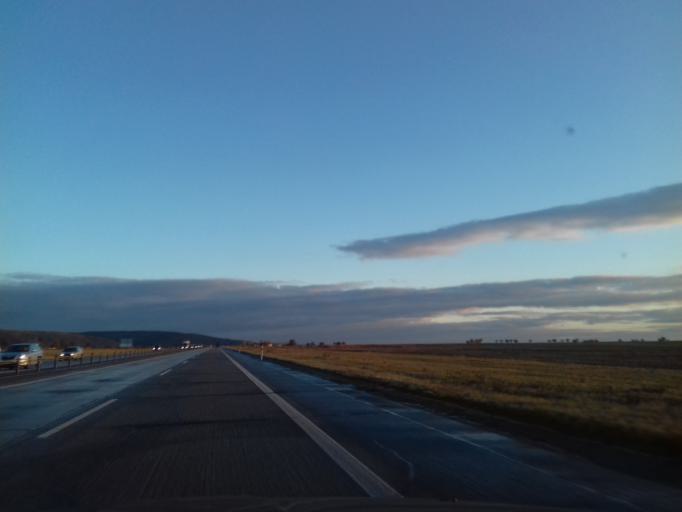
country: CZ
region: South Moravian
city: Pustimer
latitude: 49.2992
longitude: 17.0265
